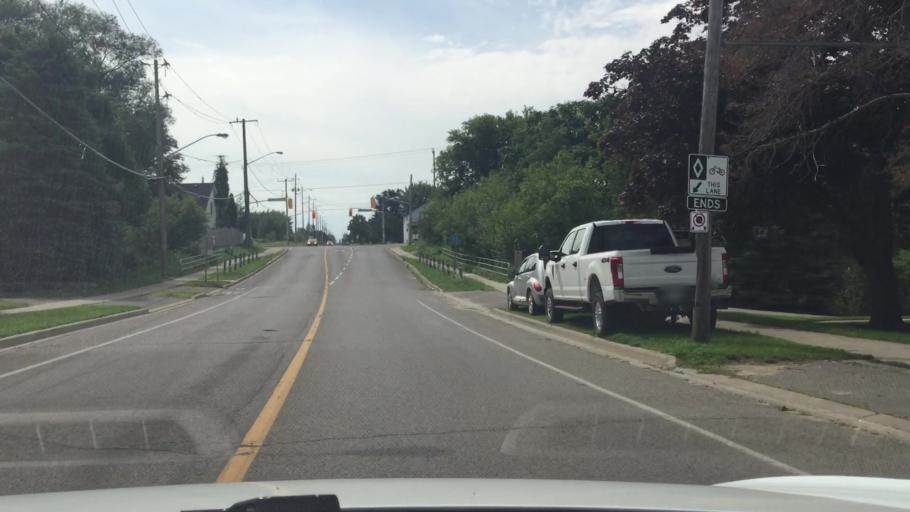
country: CA
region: Ontario
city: Oshawa
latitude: 43.9121
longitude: -78.7889
